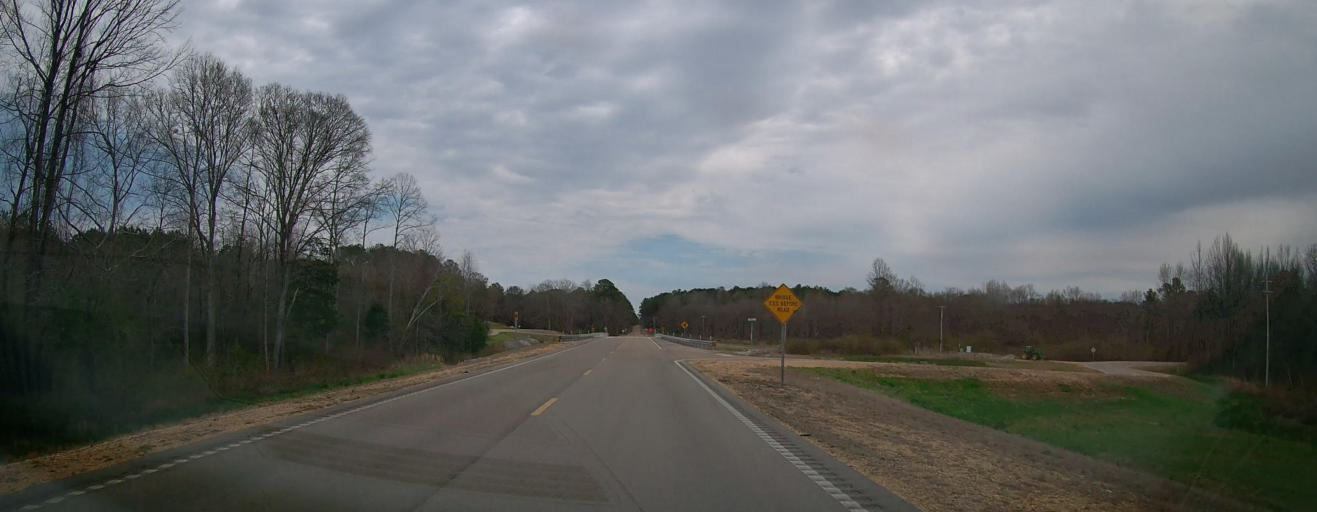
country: US
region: Mississippi
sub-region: Itawamba County
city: Fulton
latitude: 34.2208
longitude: -88.2154
